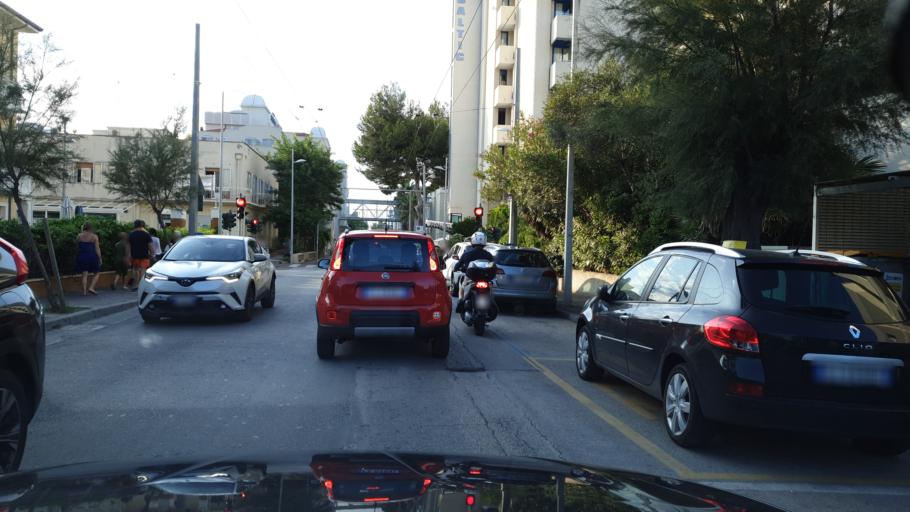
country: IT
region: Emilia-Romagna
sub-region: Provincia di Rimini
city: Riccione
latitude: 43.9963
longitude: 12.6708
